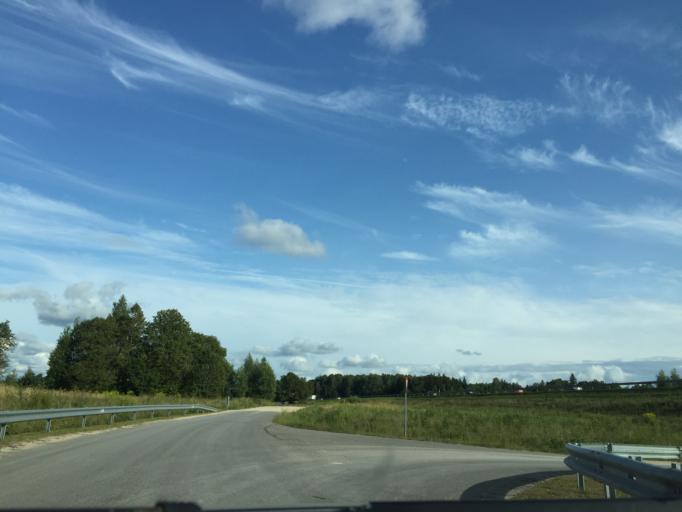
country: LV
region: Kegums
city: Kegums
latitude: 56.8242
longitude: 24.7632
